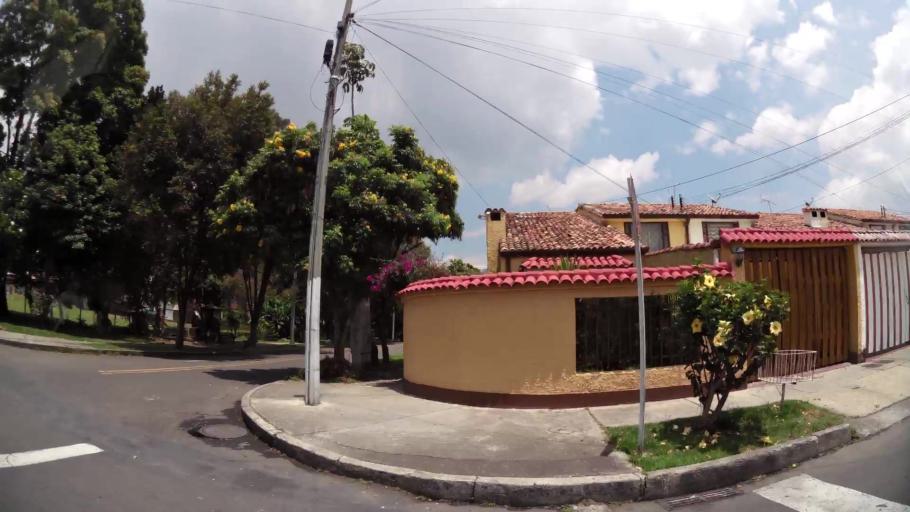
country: CO
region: Cundinamarca
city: La Calera
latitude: 4.7390
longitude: -74.0403
